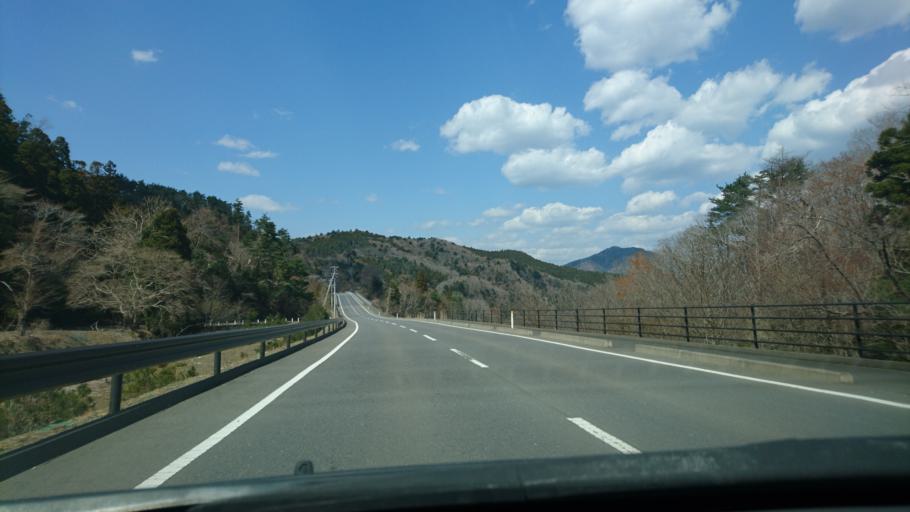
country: JP
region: Miyagi
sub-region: Oshika Gun
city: Onagawa Cho
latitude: 38.4829
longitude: 141.4929
